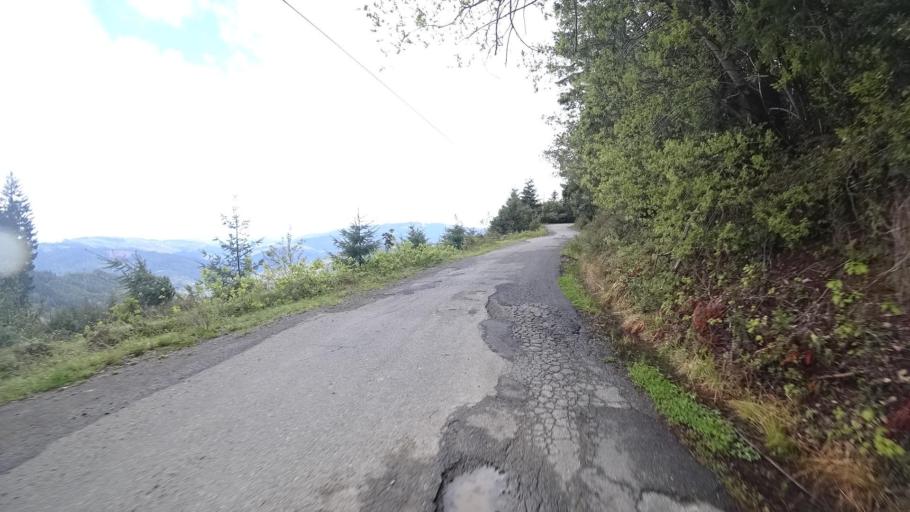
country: US
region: California
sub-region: Humboldt County
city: Blue Lake
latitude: 40.8716
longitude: -123.8939
